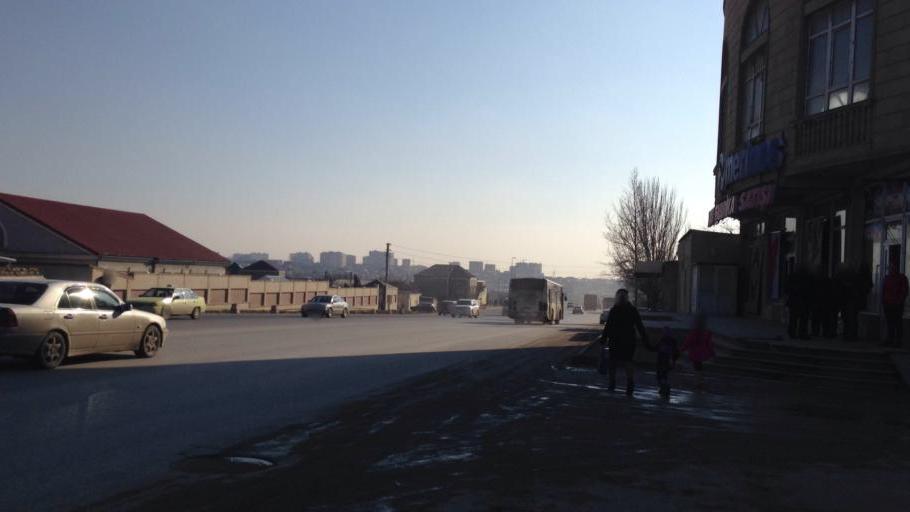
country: AZ
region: Baki
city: Sabuncu
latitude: 40.4443
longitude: 49.9338
